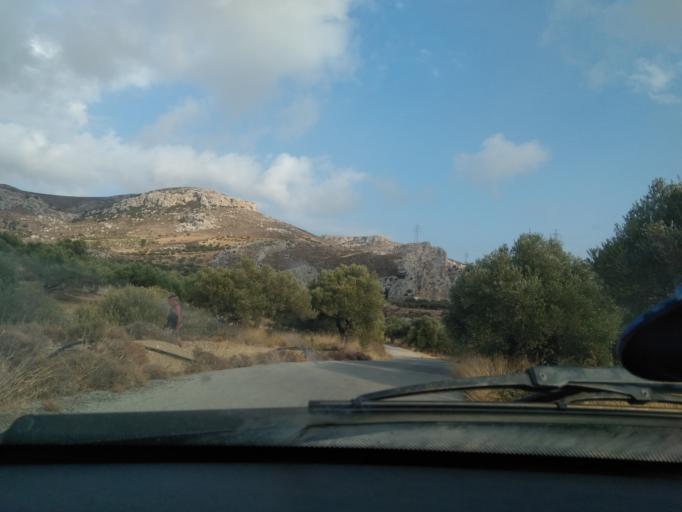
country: GR
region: Crete
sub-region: Nomos Lasithiou
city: Makry-Gialos
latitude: 35.0455
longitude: 26.0550
